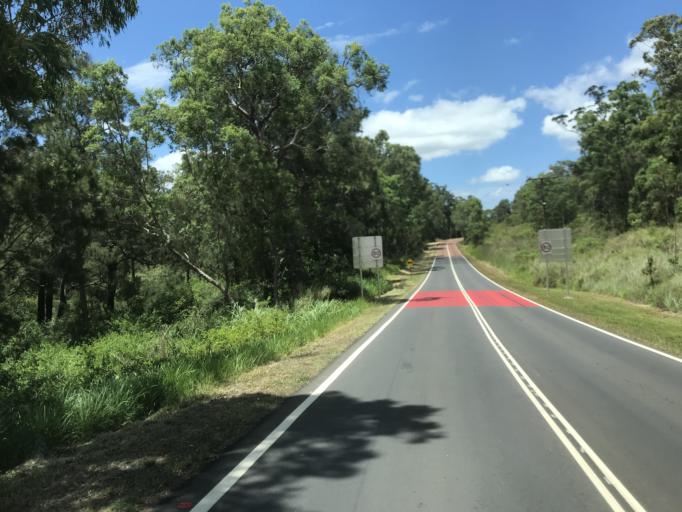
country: AU
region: Queensland
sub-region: Tablelands
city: Ravenshoe
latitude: -17.6023
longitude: 145.4785
